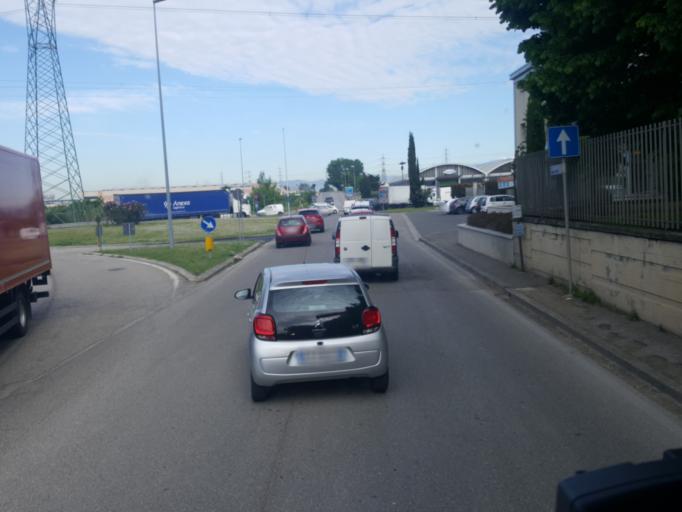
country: IT
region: Tuscany
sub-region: Province of Florence
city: Calenzano
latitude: 43.8438
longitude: 11.1600
